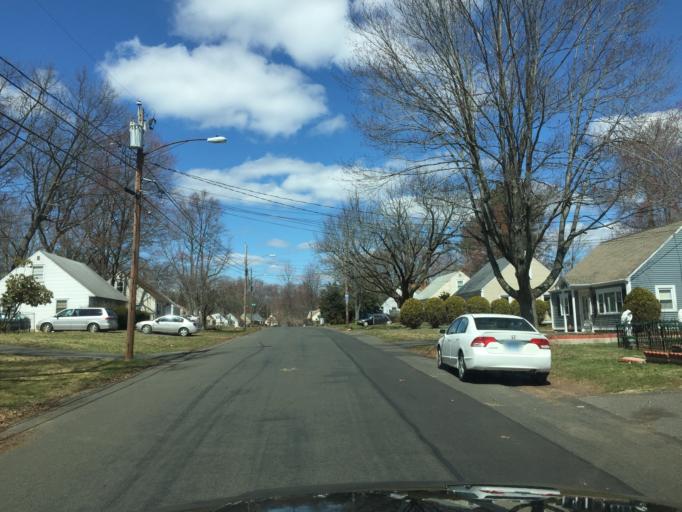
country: US
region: Connecticut
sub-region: Hartford County
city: New Britain
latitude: 41.6955
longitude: -72.7976
